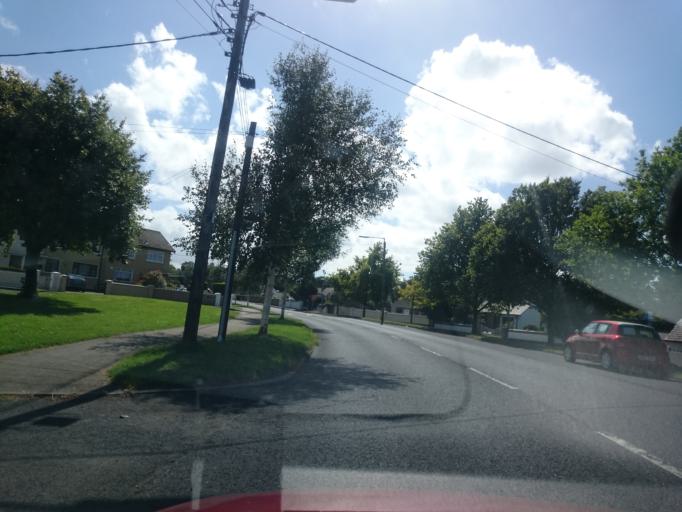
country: IE
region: Leinster
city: Clondalkin
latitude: 53.3147
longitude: -6.3976
